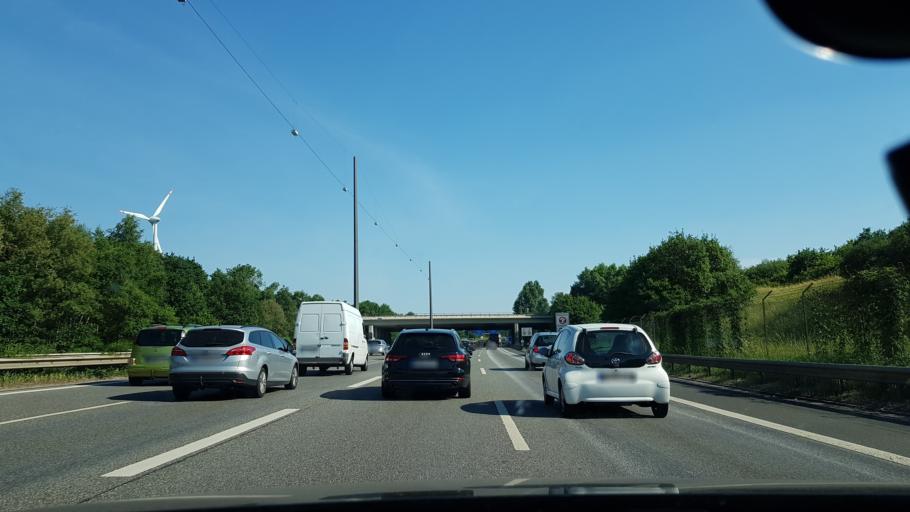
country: DE
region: Hamburg
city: Rothenburgsort
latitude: 53.5104
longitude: 10.0347
